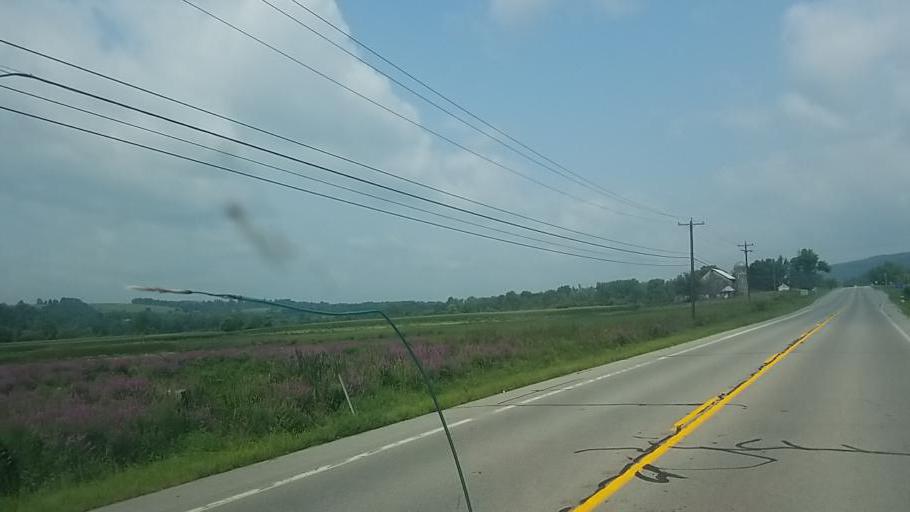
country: US
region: New York
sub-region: Montgomery County
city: Fort Plain
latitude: 42.9618
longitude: -74.6247
